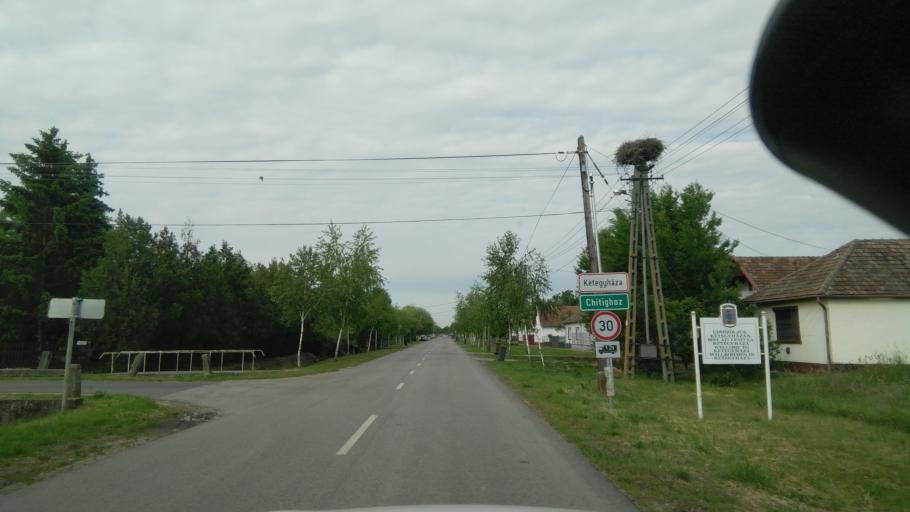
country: HU
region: Bekes
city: Ketegyhaza
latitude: 46.5534
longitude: 21.1903
